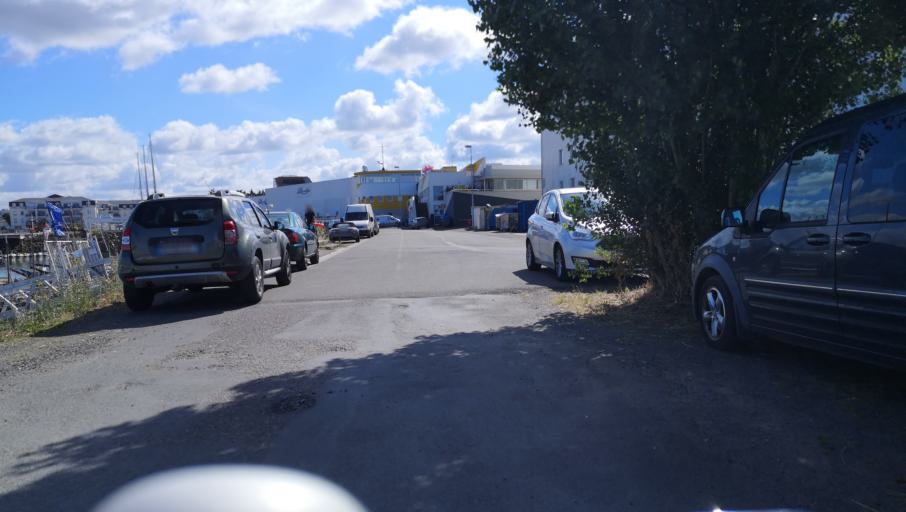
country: FR
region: Pays de la Loire
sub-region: Departement de la Vendee
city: Les Sables-d'Olonne
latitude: 46.5012
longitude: -1.7902
